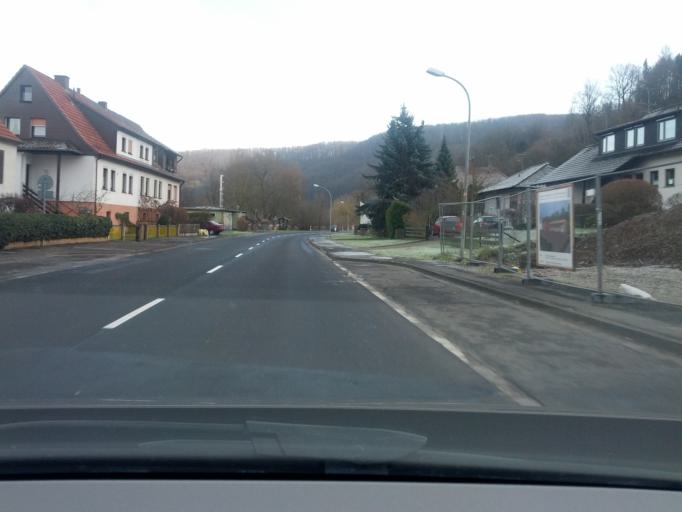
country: DE
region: Hesse
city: Witzenhausen
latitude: 51.3188
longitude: 9.8855
